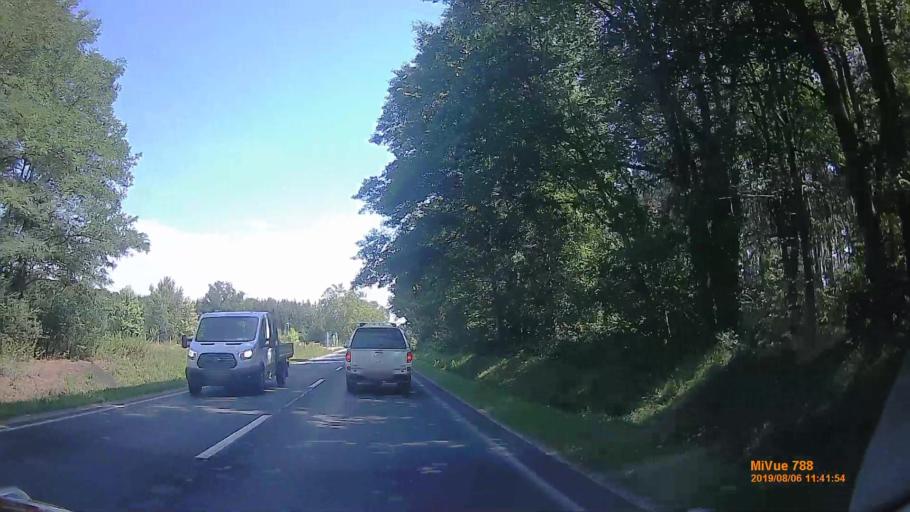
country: HU
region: Vas
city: Kormend
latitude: 46.9943
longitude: 16.5360
